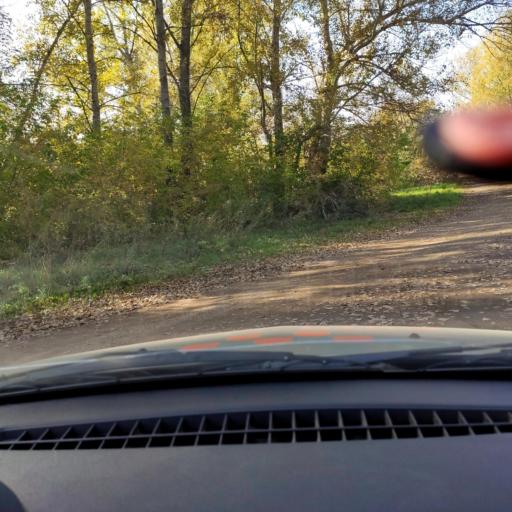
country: RU
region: Bashkortostan
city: Iglino
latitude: 54.7951
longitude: 56.2278
